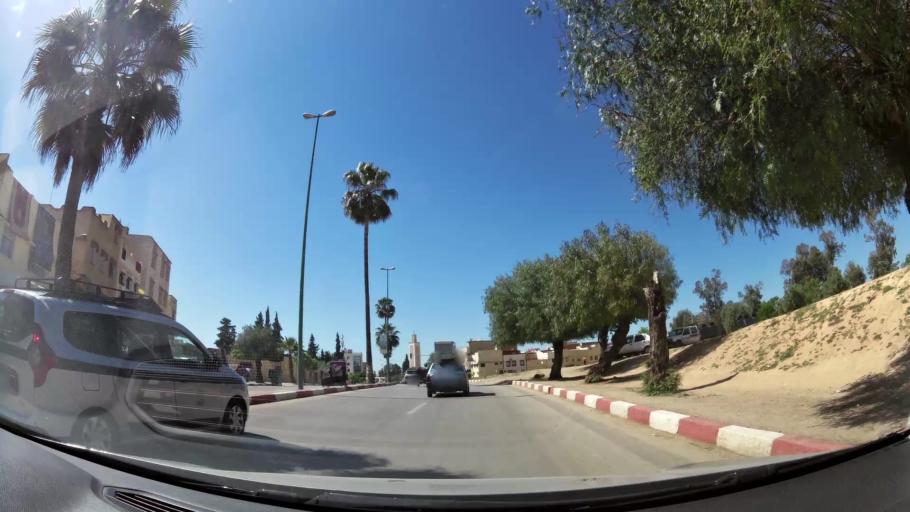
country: MA
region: Meknes-Tafilalet
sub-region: Meknes
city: Meknes
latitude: 33.8766
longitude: -5.5599
